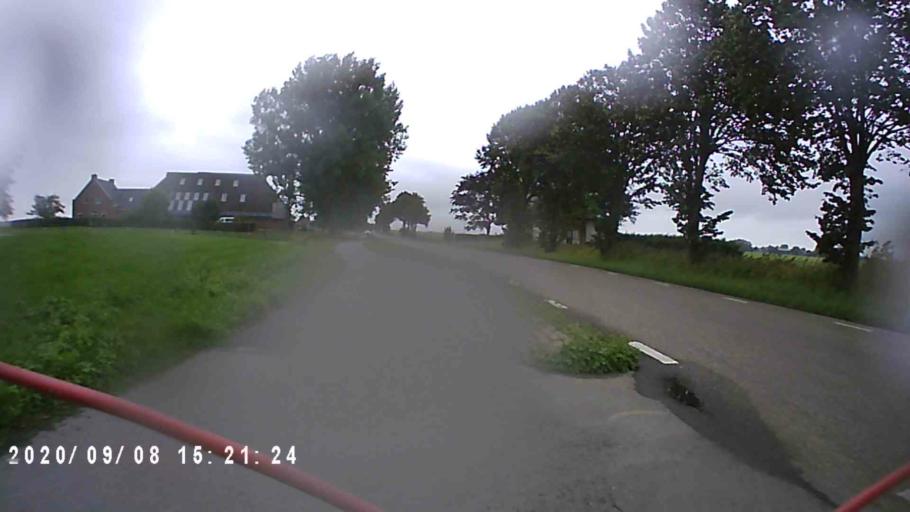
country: NL
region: Groningen
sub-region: Gemeente Bedum
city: Bedum
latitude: 53.2863
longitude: 6.6845
